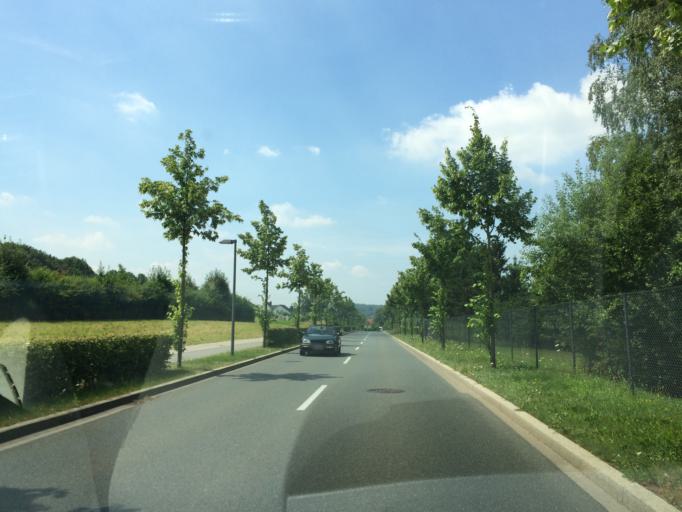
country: DE
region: North Rhine-Westphalia
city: Hemer
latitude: 51.3827
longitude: 7.7835
